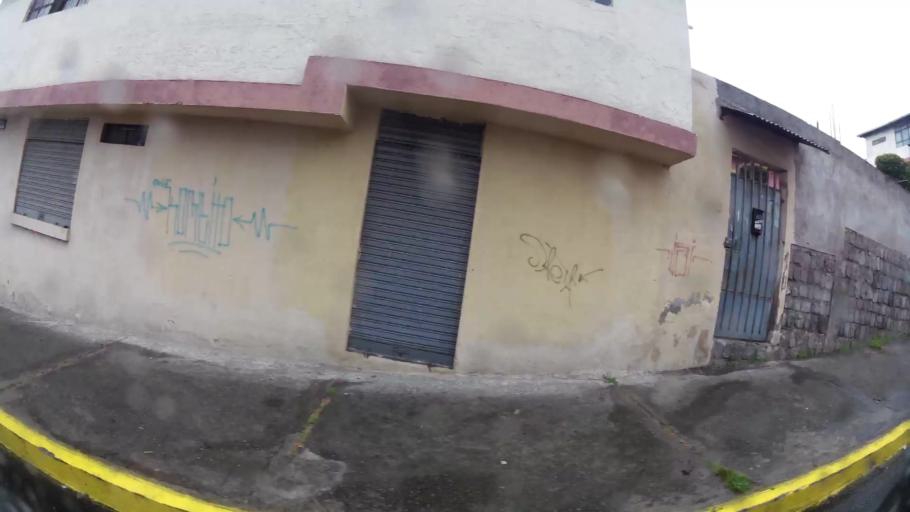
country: EC
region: Pichincha
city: Quito
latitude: -0.1198
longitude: -78.5026
